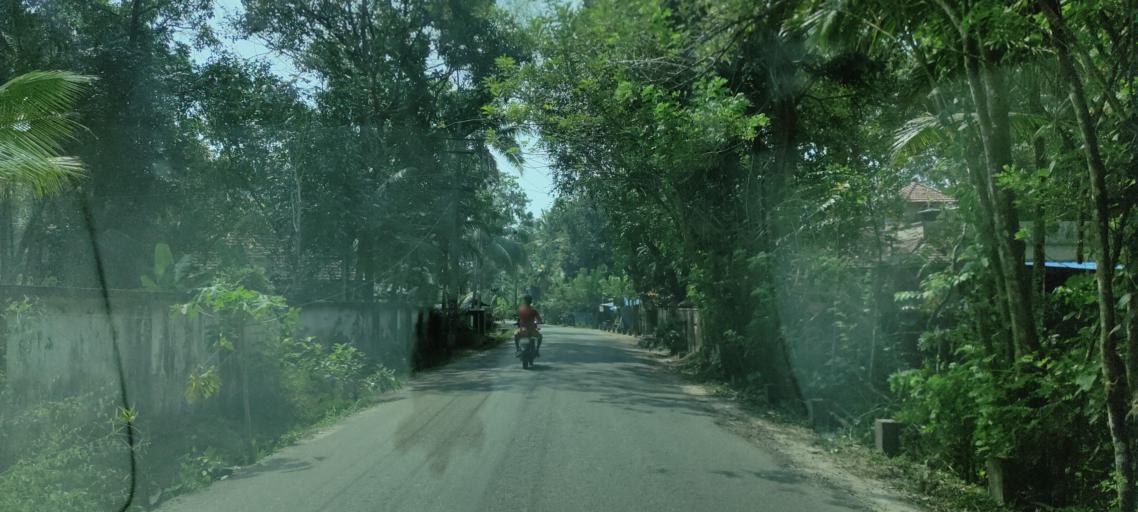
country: IN
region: Kerala
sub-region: Alappuzha
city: Shertallai
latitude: 9.6554
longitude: 76.3583
